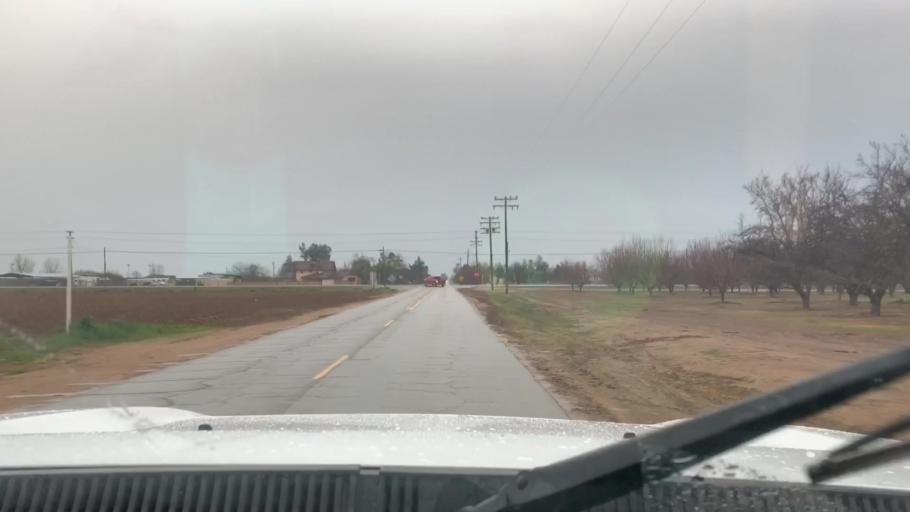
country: US
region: California
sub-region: Kern County
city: Shafter
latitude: 35.4780
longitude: -119.2592
